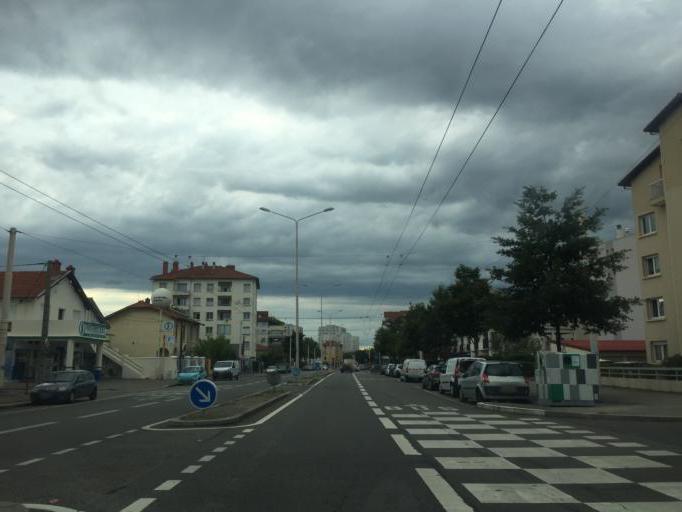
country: FR
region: Rhone-Alpes
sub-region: Departement du Rhone
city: Venissieux
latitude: 45.7256
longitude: 4.8812
